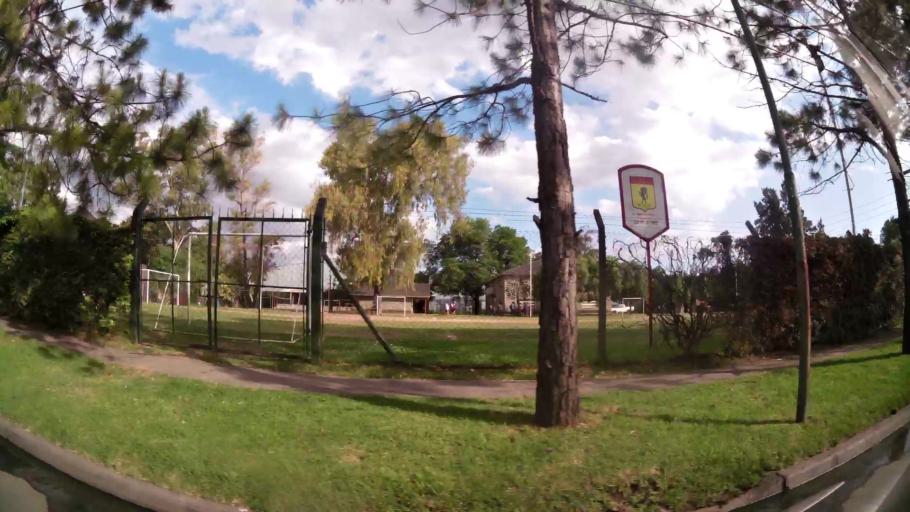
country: AR
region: Buenos Aires
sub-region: Partido de Tigre
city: Tigre
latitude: -34.4706
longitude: -58.6589
